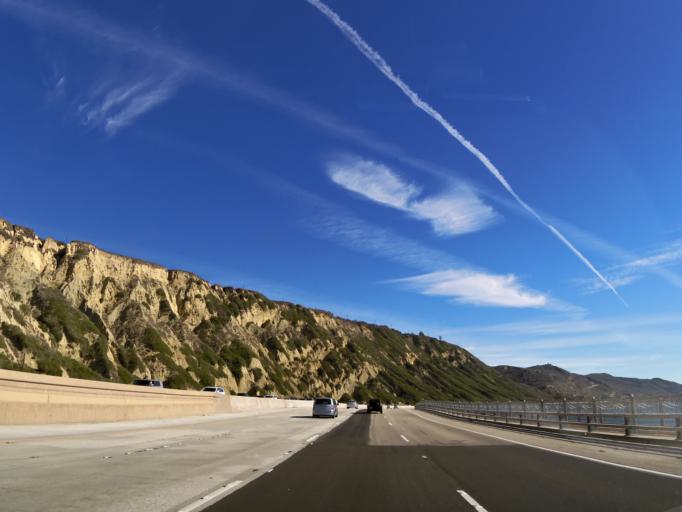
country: US
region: California
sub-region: Santa Barbara County
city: Carpinteria
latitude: 34.3562
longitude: -119.4357
